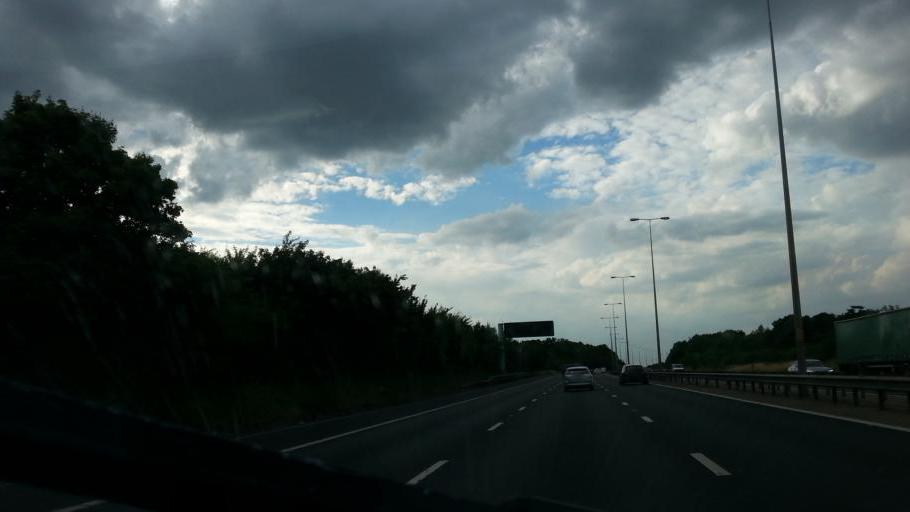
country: GB
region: England
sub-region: Worcestershire
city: Upton upon Severn
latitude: 52.0934
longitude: -2.1835
